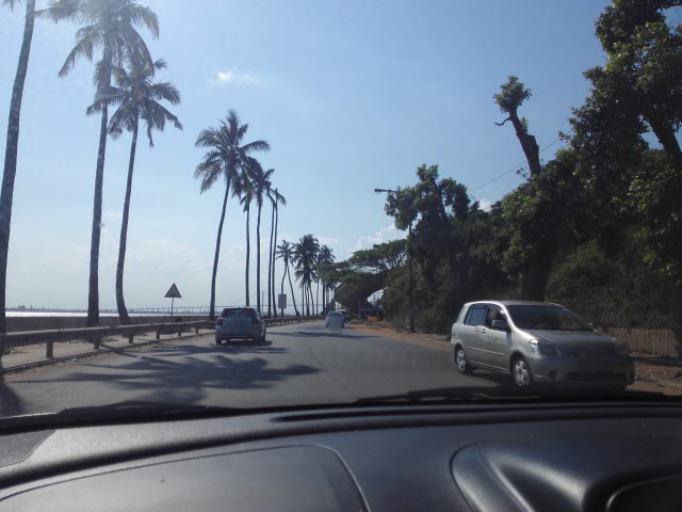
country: MZ
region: Maputo City
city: Maputo
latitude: -25.9841
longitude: 32.5892
